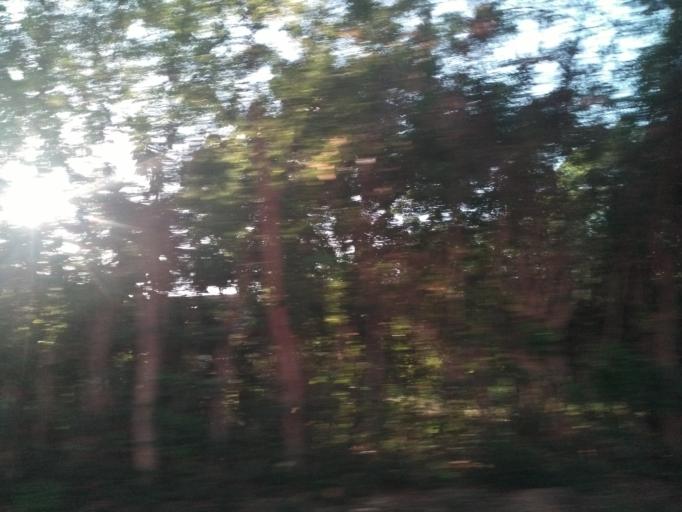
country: TZ
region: Dar es Salaam
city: Magomeni
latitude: -6.7612
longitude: 39.2812
